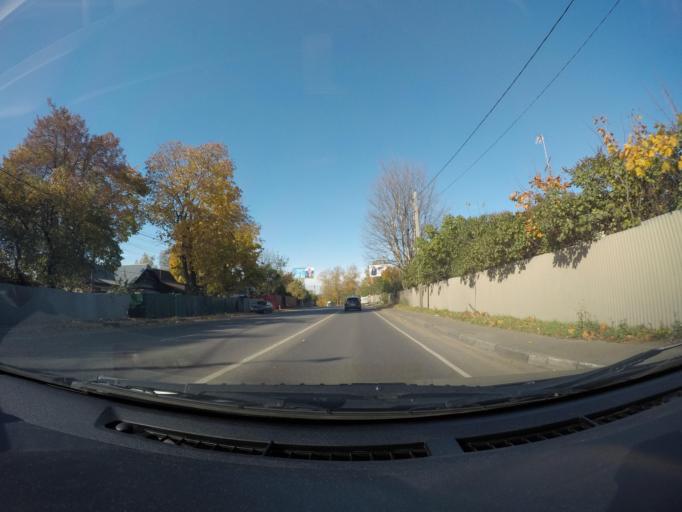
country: RU
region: Moskovskaya
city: Kraskovo
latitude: 55.6329
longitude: 37.9698
